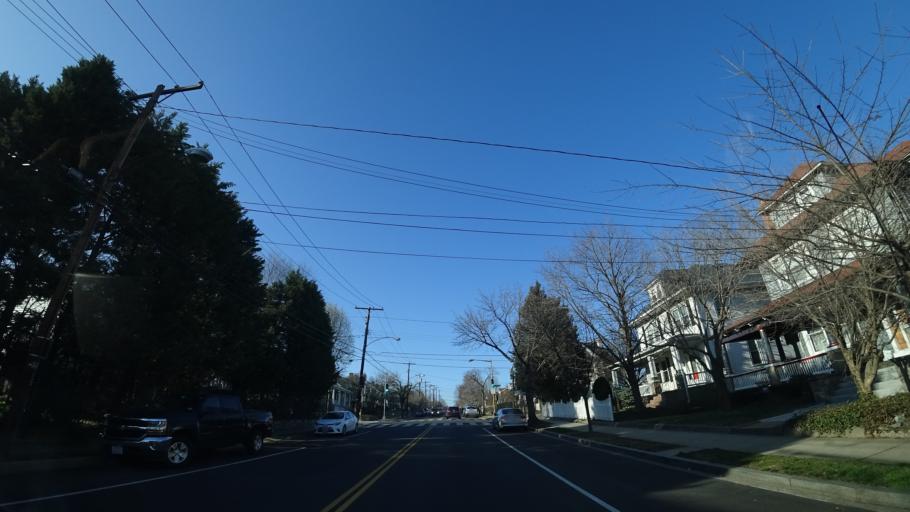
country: US
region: Maryland
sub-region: Montgomery County
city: Takoma Park
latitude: 38.9515
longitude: -77.0297
